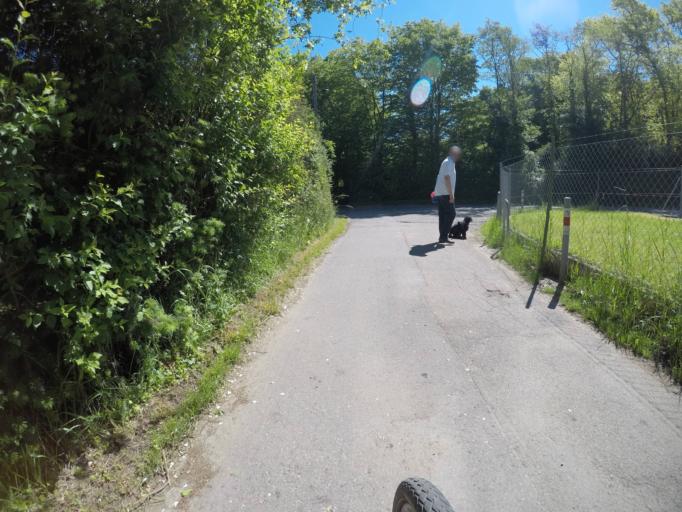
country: DE
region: Baden-Wuerttemberg
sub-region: Karlsruhe Region
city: Pforzheim
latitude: 48.9036
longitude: 8.6914
